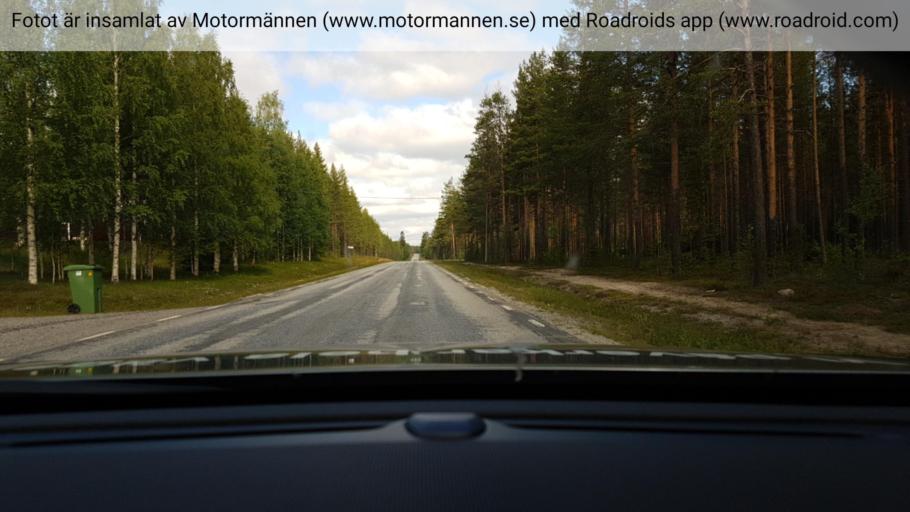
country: SE
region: Vaesterbotten
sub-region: Lycksele Kommun
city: Lycksele
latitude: 64.8322
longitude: 18.7814
